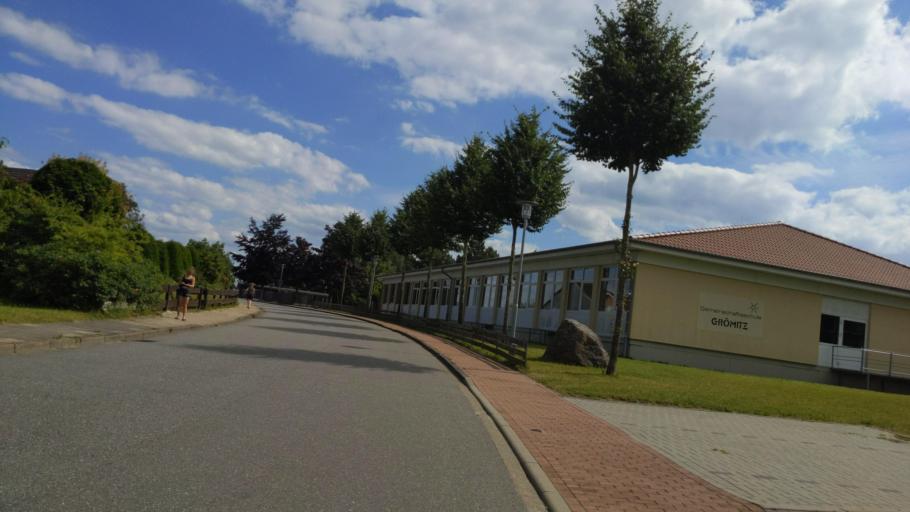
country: DE
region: Schleswig-Holstein
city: Gromitz
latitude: 54.1462
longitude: 10.9510
